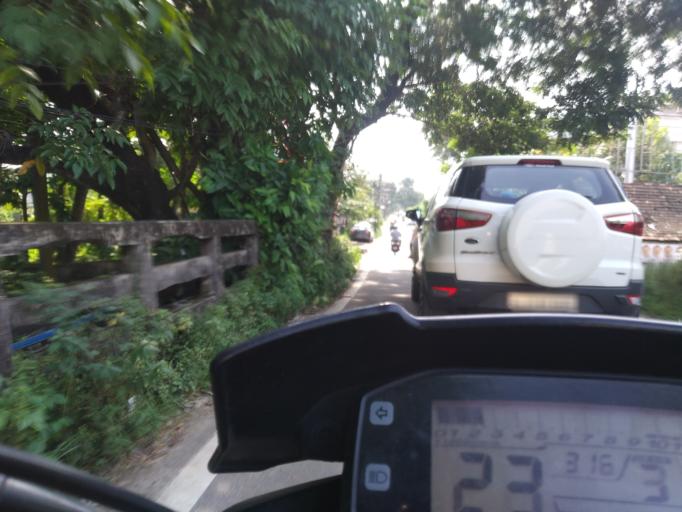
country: IN
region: Kerala
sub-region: Ernakulam
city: Cochin
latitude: 9.9837
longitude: 76.3026
